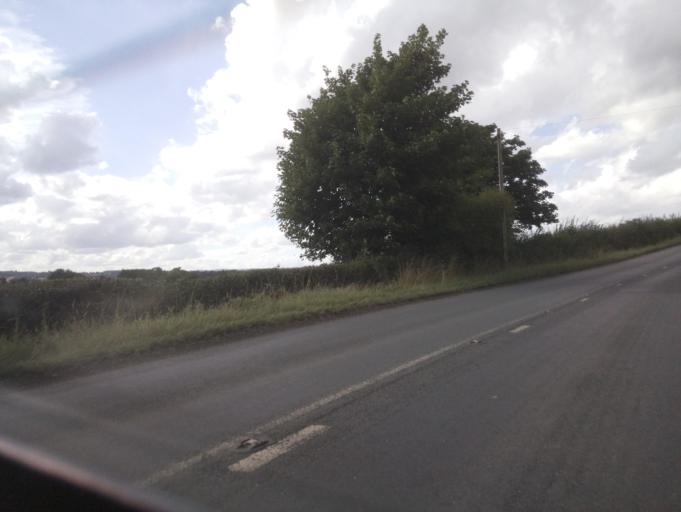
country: GB
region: England
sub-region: North Yorkshire
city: Bedale
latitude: 54.2146
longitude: -1.6291
